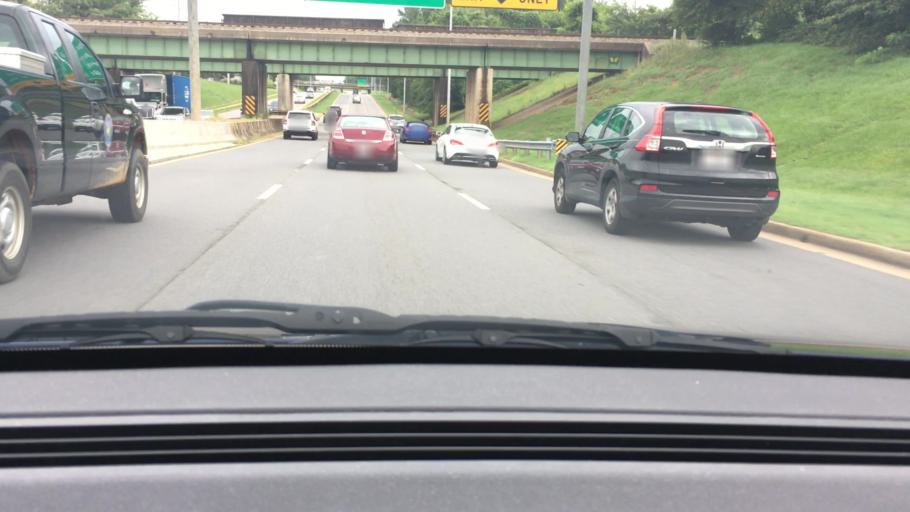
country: US
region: Alabama
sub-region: Tuscaloosa County
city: Tuscaloosa
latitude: 33.2014
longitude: -87.5252
